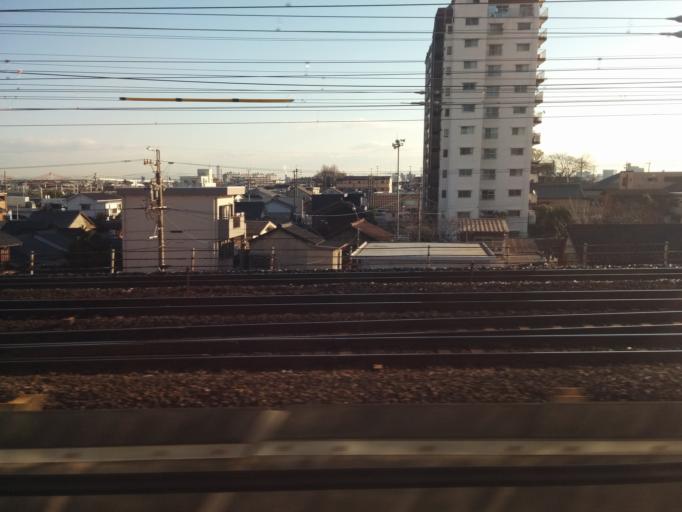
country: JP
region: Aichi
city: Nagoya-shi
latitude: 35.1937
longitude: 136.8649
